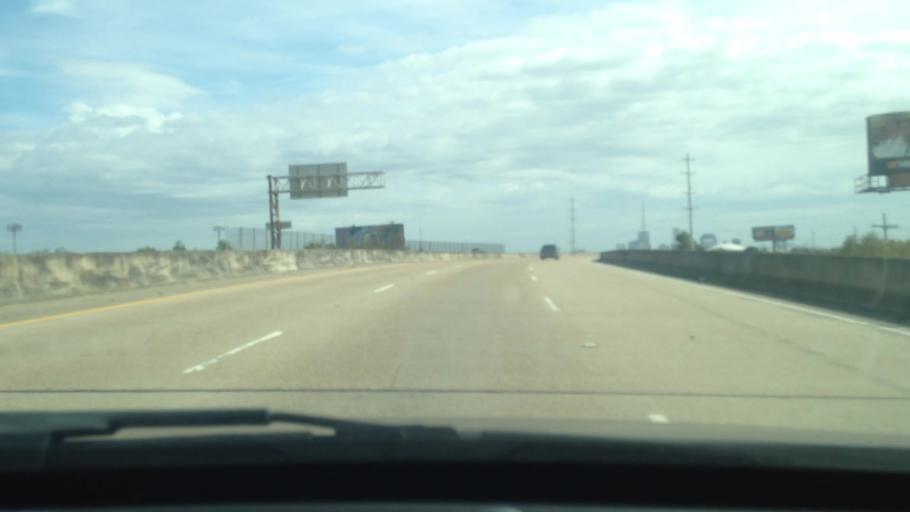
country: US
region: Louisiana
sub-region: Jefferson Parish
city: Jefferson
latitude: 29.9691
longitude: -90.1330
